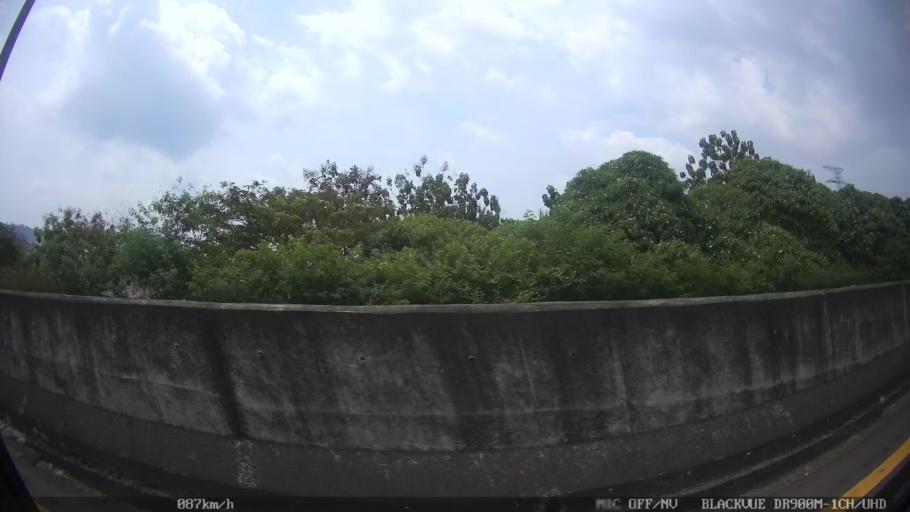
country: ID
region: Banten
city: Curug
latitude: -5.9830
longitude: 106.0319
